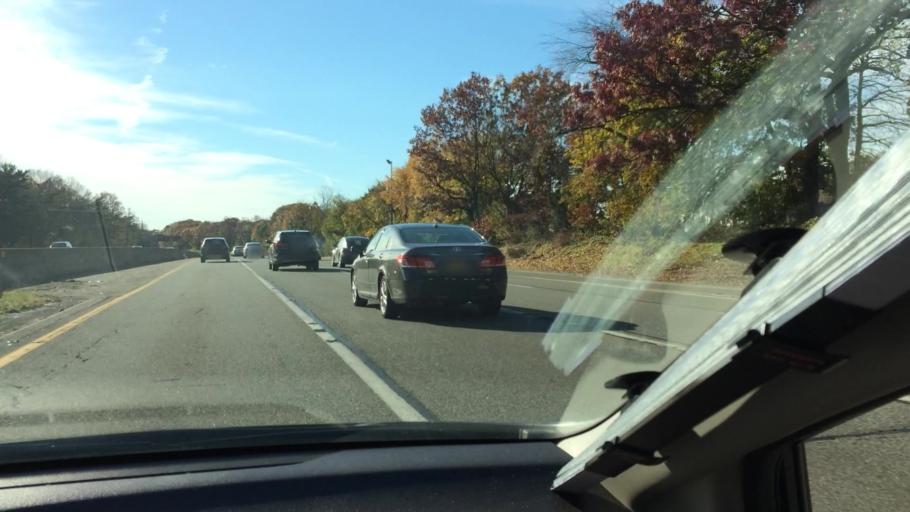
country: US
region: New York
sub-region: Nassau County
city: North Valley Stream
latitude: 40.6829
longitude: -73.6898
